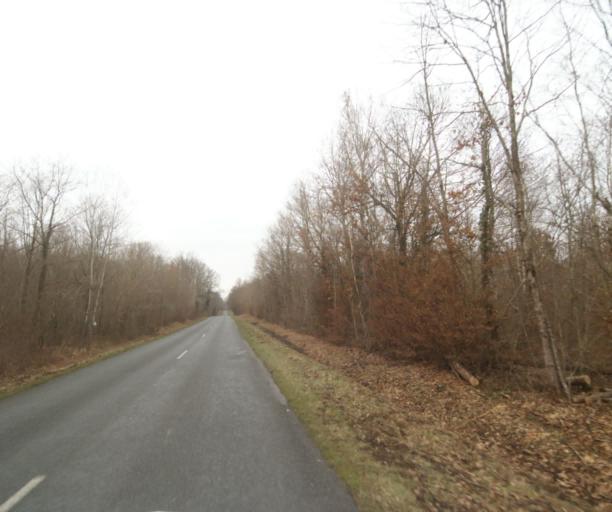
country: FR
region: Champagne-Ardenne
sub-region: Departement de la Marne
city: Pargny-sur-Saulx
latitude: 48.7240
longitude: 4.8725
